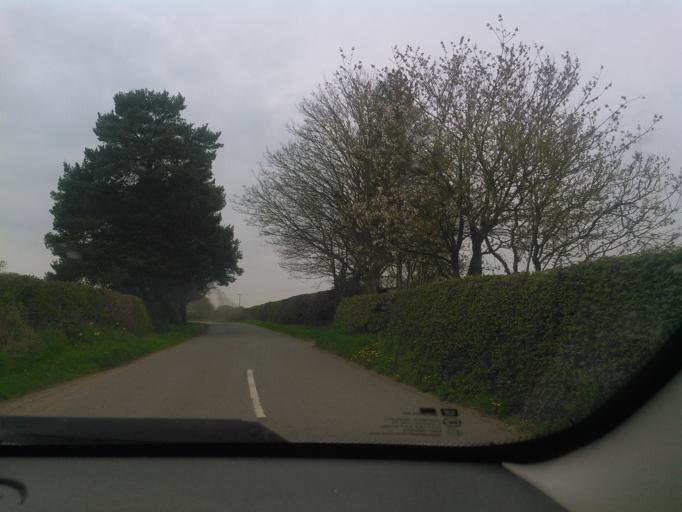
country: GB
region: England
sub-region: Shropshire
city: Shawbury
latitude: 52.8066
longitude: -2.6198
